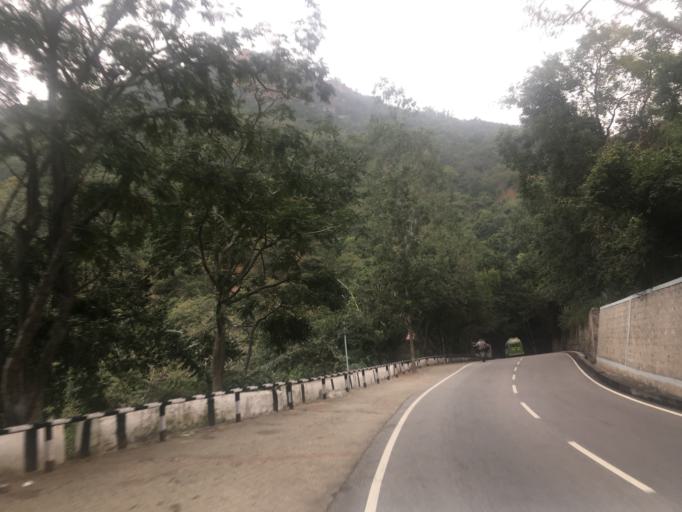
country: IN
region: Andhra Pradesh
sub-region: Chittoor
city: Tirumala
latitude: 13.6628
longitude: 79.3511
